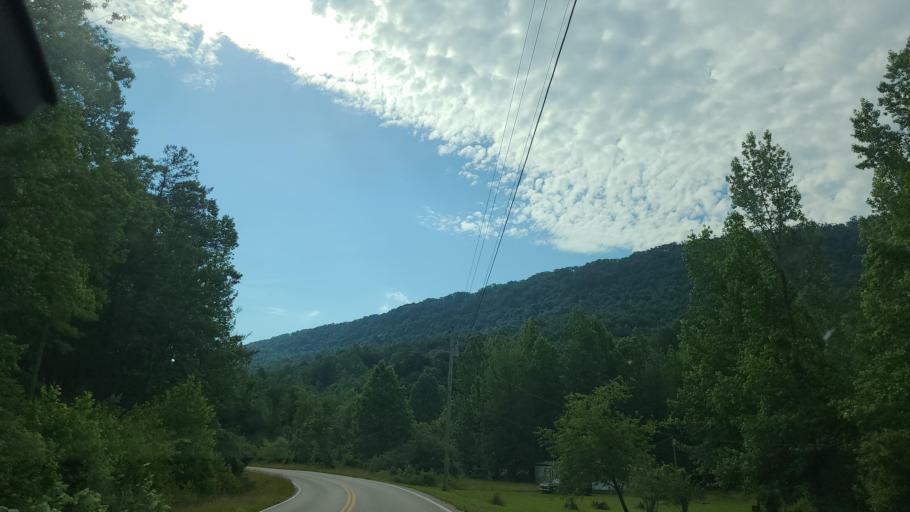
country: US
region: Kentucky
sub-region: Knox County
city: Barbourville
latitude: 36.6794
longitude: -83.9050
